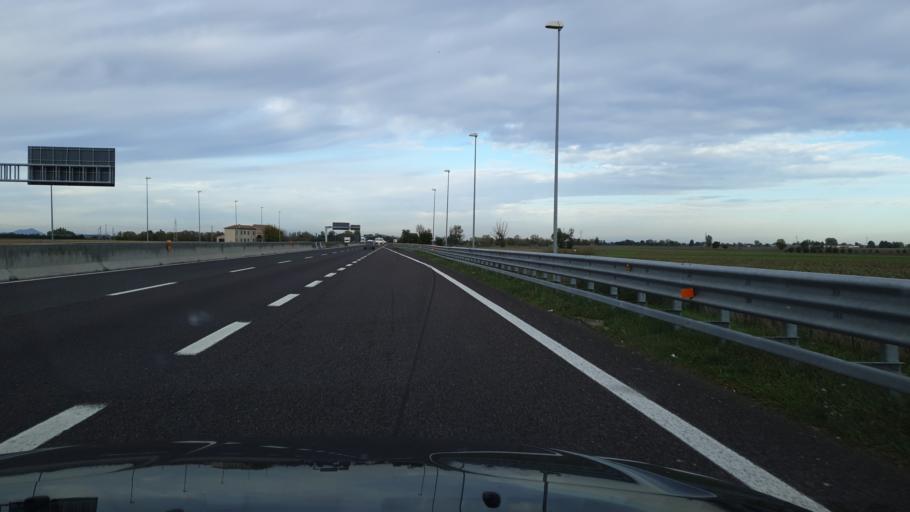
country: IT
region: Veneto
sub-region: Provincia di Rovigo
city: Villamarzana
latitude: 45.0246
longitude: 11.6962
